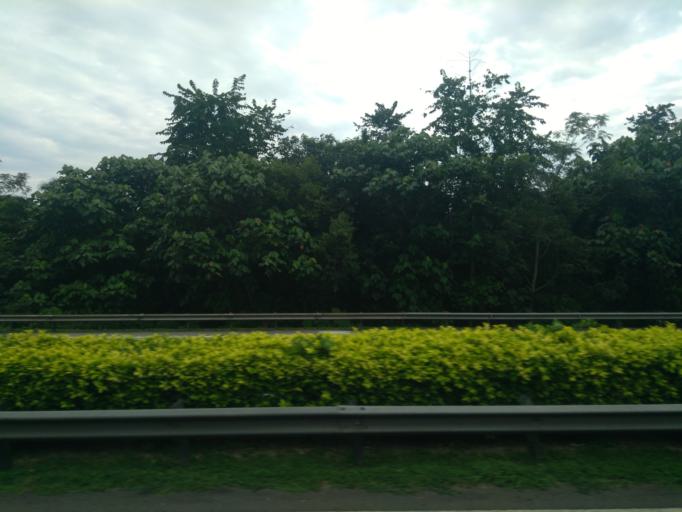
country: MY
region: Negeri Sembilan
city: Tampin
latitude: 2.4582
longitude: 102.1632
